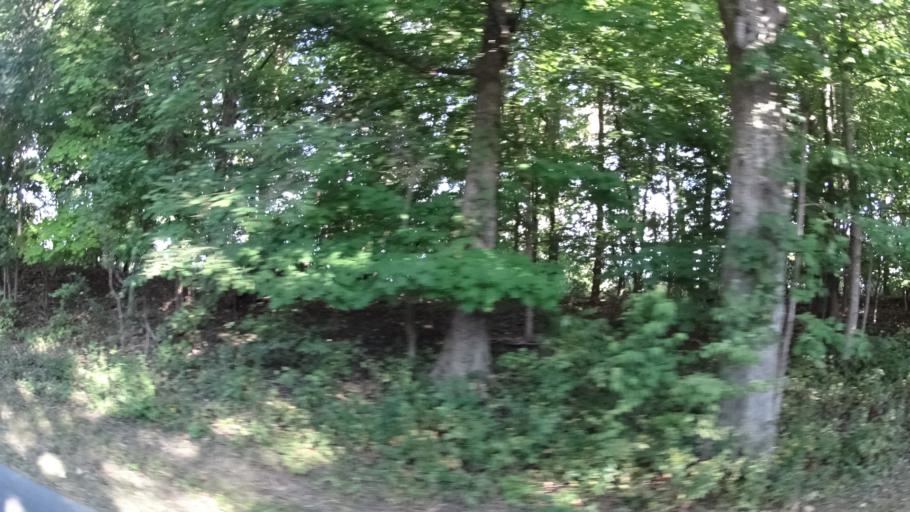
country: US
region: Ohio
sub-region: Erie County
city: Sandusky
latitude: 41.6139
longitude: -82.7131
